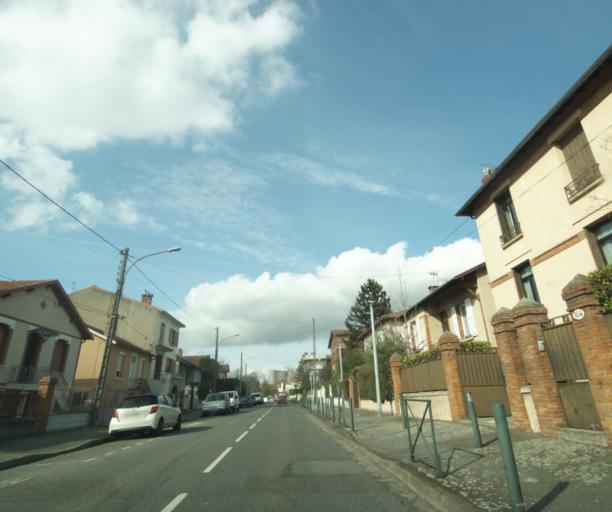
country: FR
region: Midi-Pyrenees
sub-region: Departement de la Haute-Garonne
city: Toulouse
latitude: 43.5991
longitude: 1.4726
